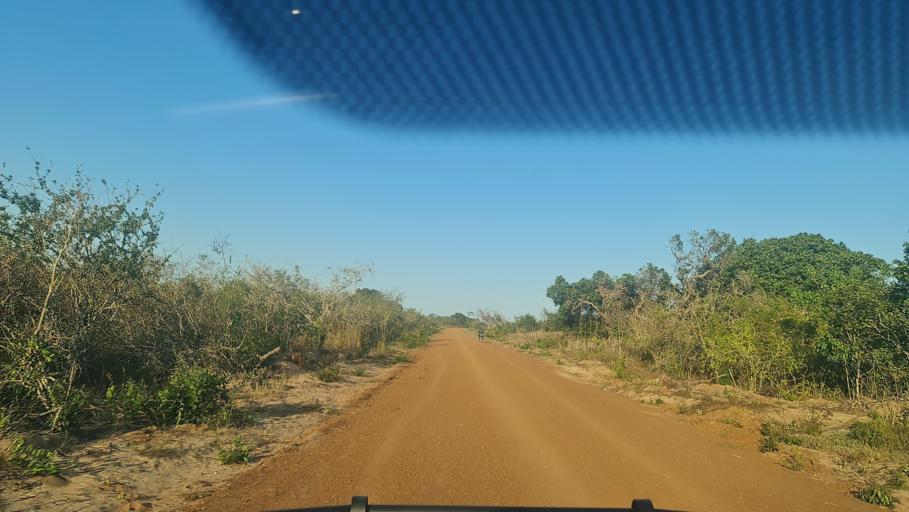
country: MZ
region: Nampula
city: Antonio Enes
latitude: -15.7080
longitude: 40.2532
